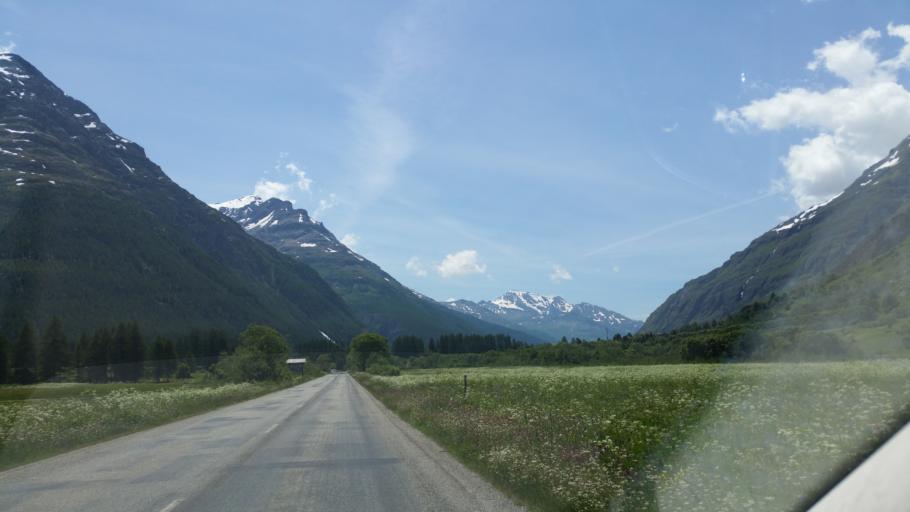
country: FR
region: Rhone-Alpes
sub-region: Departement de la Savoie
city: Val-d'Isere
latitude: 45.3372
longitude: 7.0219
